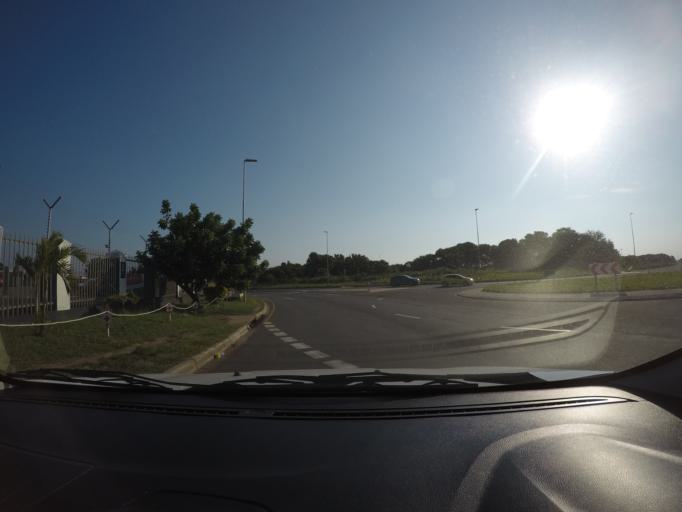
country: ZA
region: KwaZulu-Natal
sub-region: uThungulu District Municipality
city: Richards Bay
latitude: -28.7334
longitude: 32.0361
